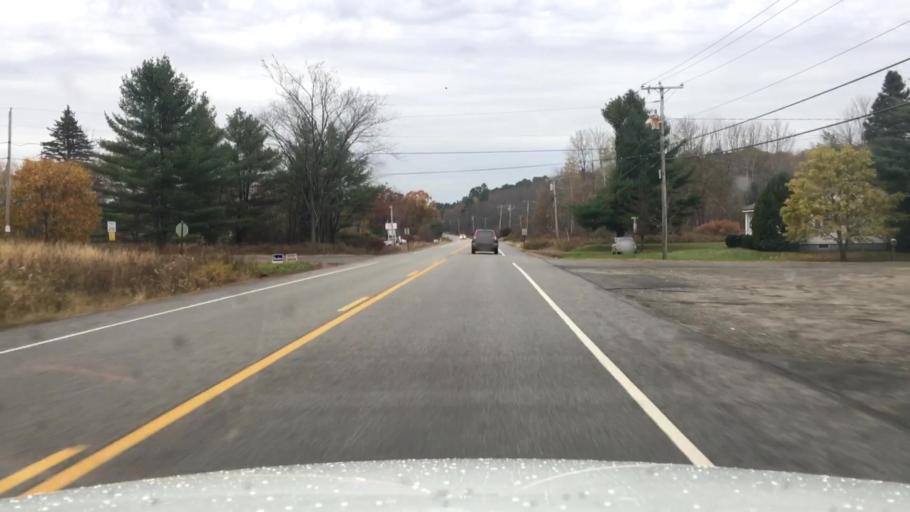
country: US
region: Maine
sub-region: Kennebec County
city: Pittston
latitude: 44.2135
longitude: -69.7556
